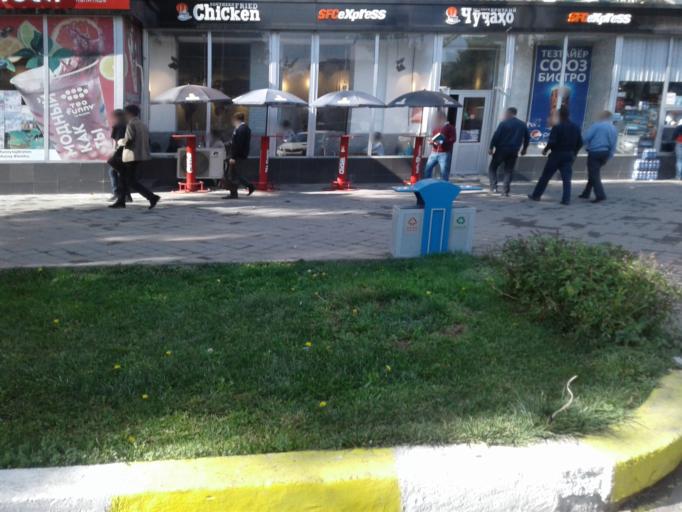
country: TJ
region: Dushanbe
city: Dushanbe
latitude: 38.5683
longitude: 68.7934
